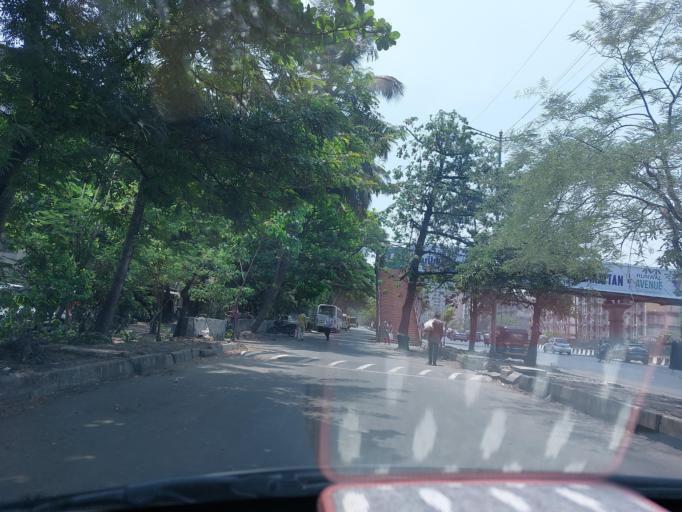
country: IN
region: Maharashtra
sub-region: Mumbai Suburban
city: Powai
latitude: 19.1178
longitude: 72.9362
